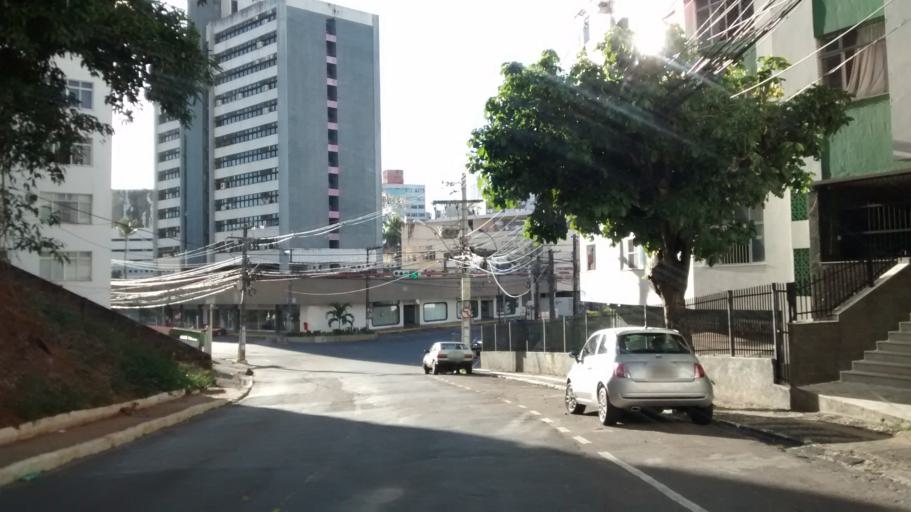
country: BR
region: Bahia
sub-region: Salvador
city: Salvador
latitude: -13.0059
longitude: -38.5215
